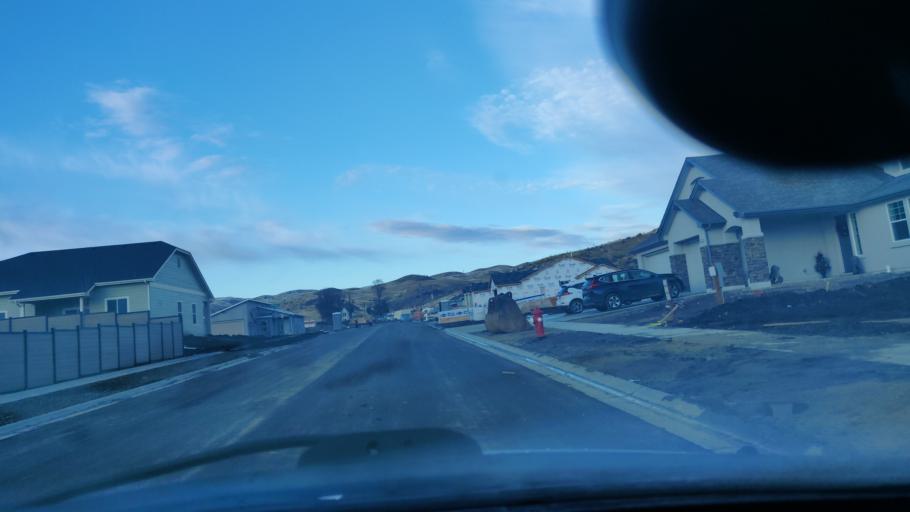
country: US
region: Idaho
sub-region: Ada County
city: Eagle
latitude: 43.7905
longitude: -116.2596
